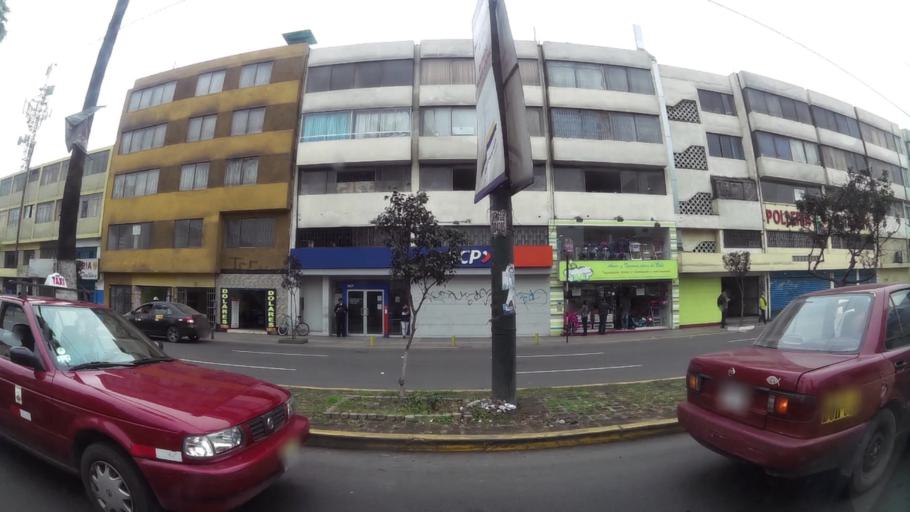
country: PE
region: Lima
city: Lima
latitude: -12.0650
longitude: -77.0291
